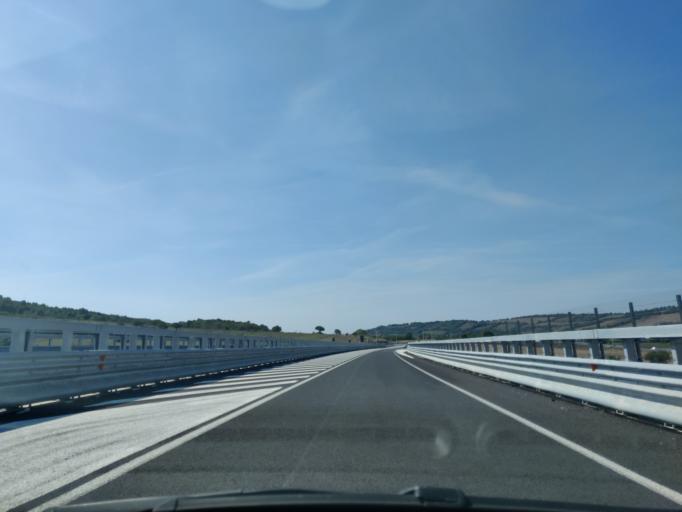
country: IT
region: Latium
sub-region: Provincia di Viterbo
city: Monte Romano
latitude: 42.2827
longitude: 11.9290
